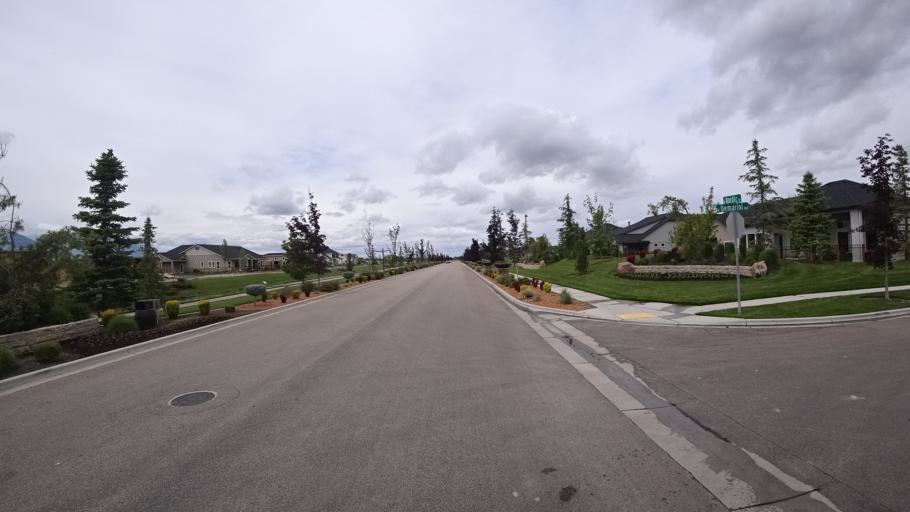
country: US
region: Idaho
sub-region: Ada County
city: Star
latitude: 43.7030
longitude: -116.4341
